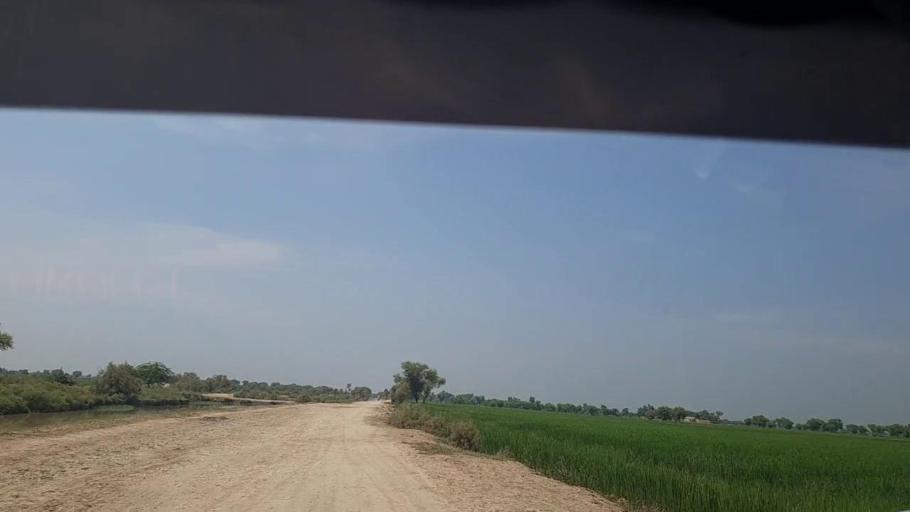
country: PK
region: Sindh
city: Thul
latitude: 28.1948
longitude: 68.7080
